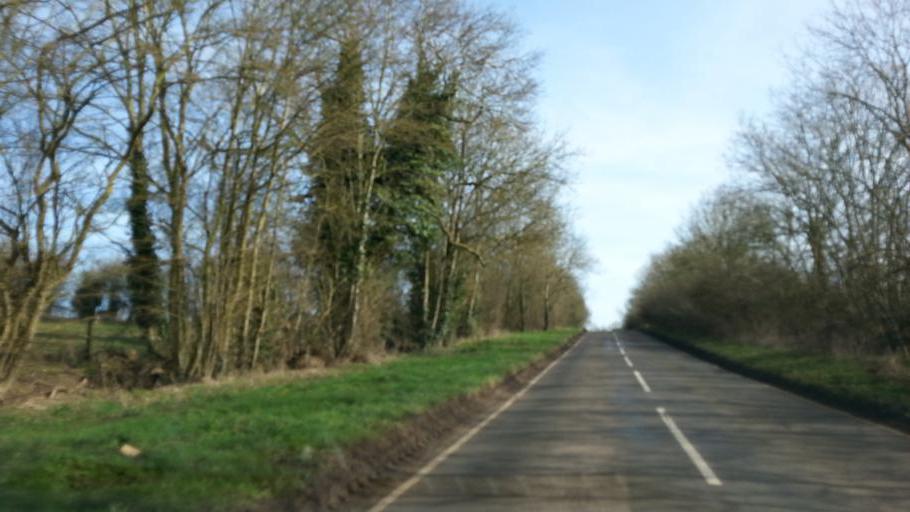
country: GB
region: England
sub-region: Northamptonshire
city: Brixworth
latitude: 52.3276
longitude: -0.9364
